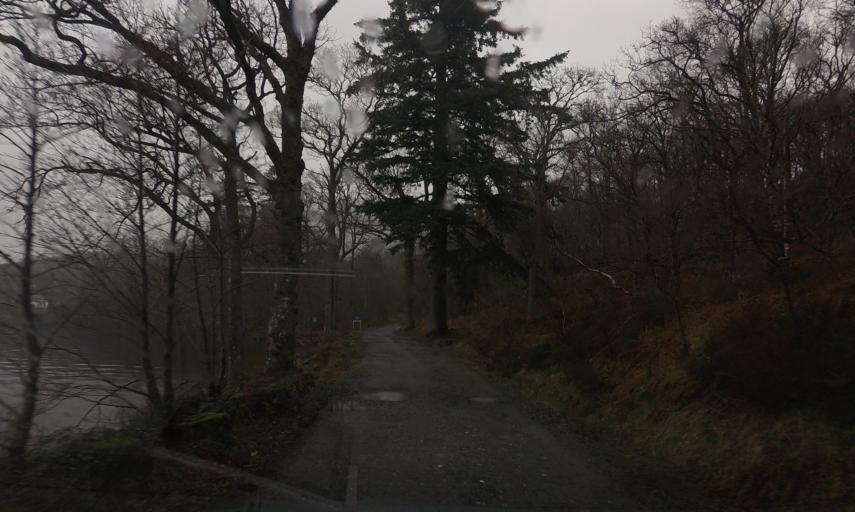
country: GB
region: Scotland
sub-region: West Dunbartonshire
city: Balloch
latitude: 56.1556
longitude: -4.6425
